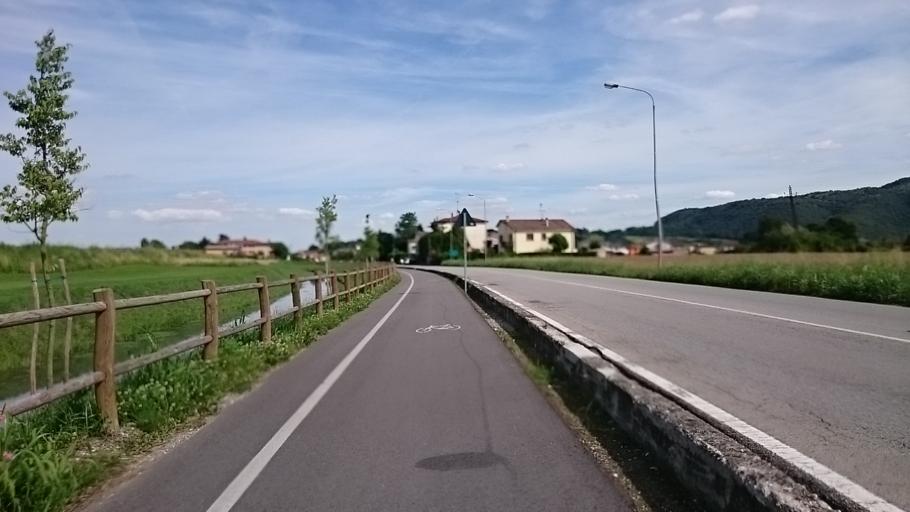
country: IT
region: Veneto
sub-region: Provincia di Vicenza
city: Arcugnano-Torri
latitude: 45.5011
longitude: 11.5770
